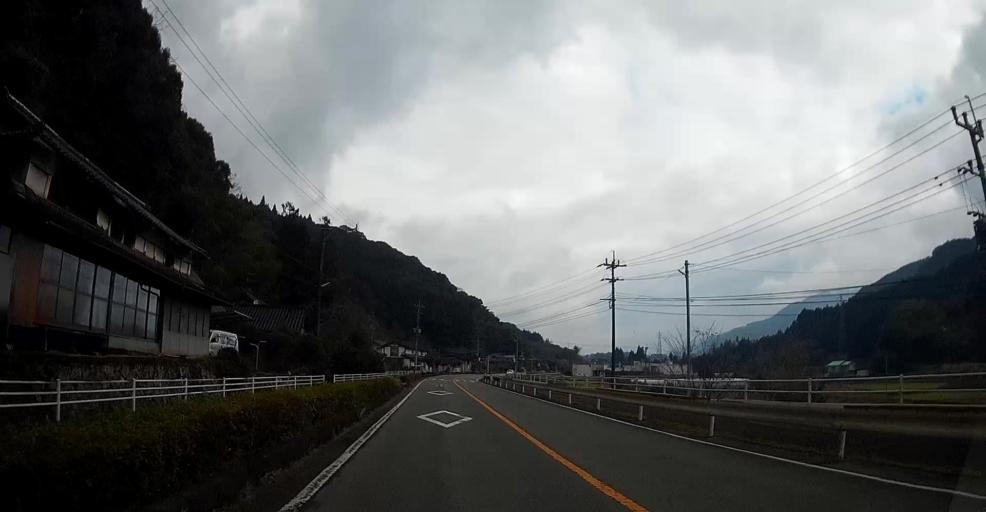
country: JP
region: Kumamoto
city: Matsubase
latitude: 32.6144
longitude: 130.8470
